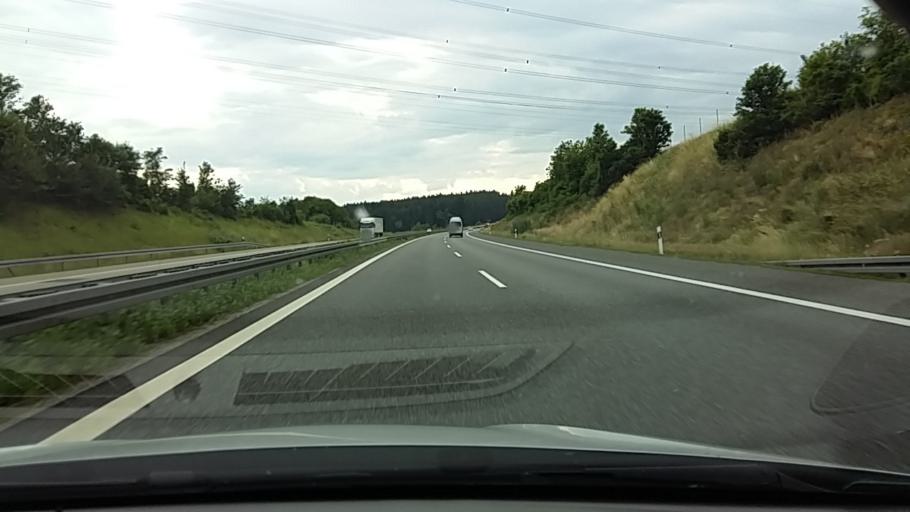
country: DE
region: Bavaria
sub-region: Upper Palatinate
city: Moosbach
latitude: 49.6116
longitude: 12.3984
